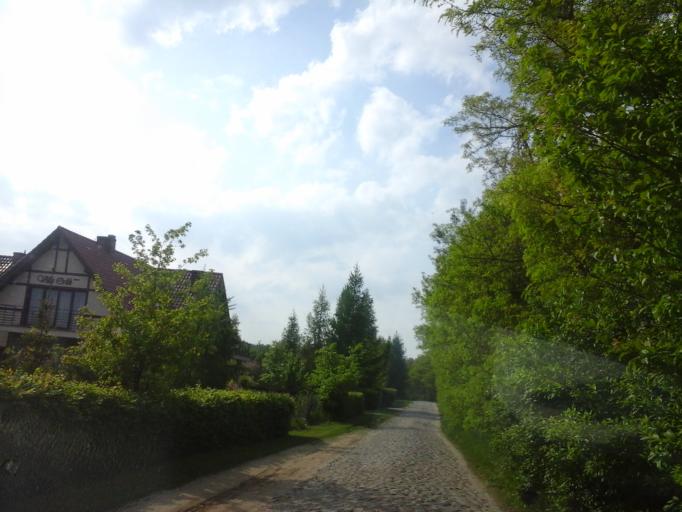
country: PL
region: West Pomeranian Voivodeship
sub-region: Powiat mysliborski
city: Barlinek
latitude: 53.0443
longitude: 15.2119
